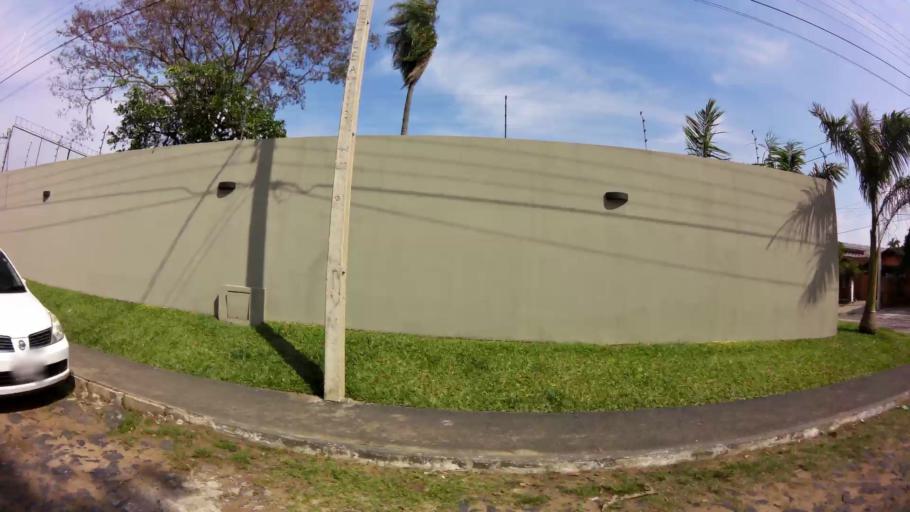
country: PY
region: Central
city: Fernando de la Mora
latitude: -25.2620
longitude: -57.5521
